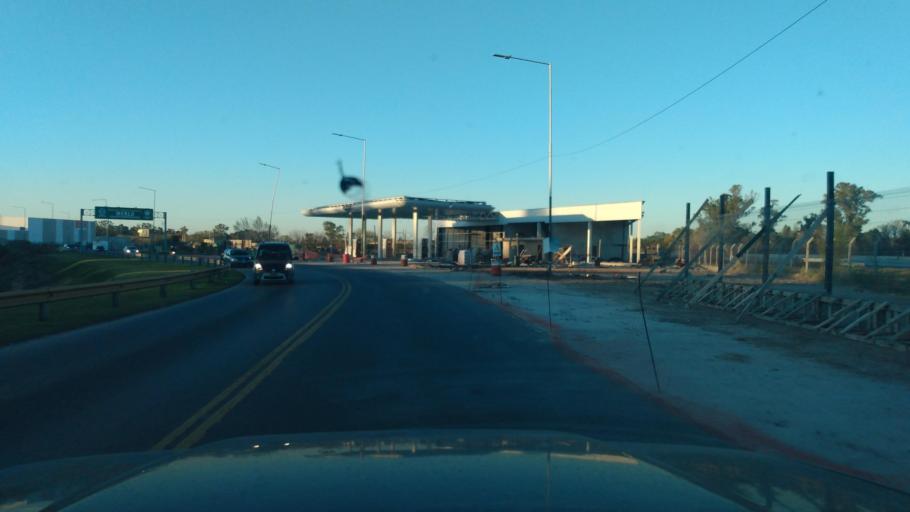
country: AR
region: Buenos Aires
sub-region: Partido de Merlo
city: Merlo
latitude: -34.6337
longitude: -58.7270
